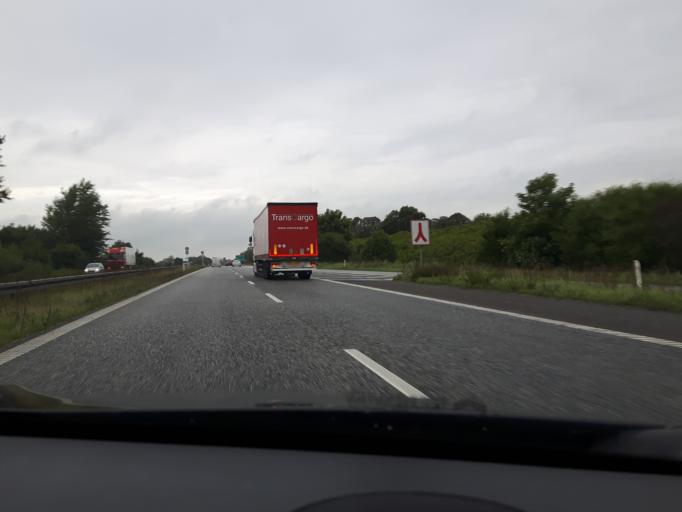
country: DK
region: Central Jutland
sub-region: Randers Kommune
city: Randers
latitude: 56.4318
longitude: 10.0348
